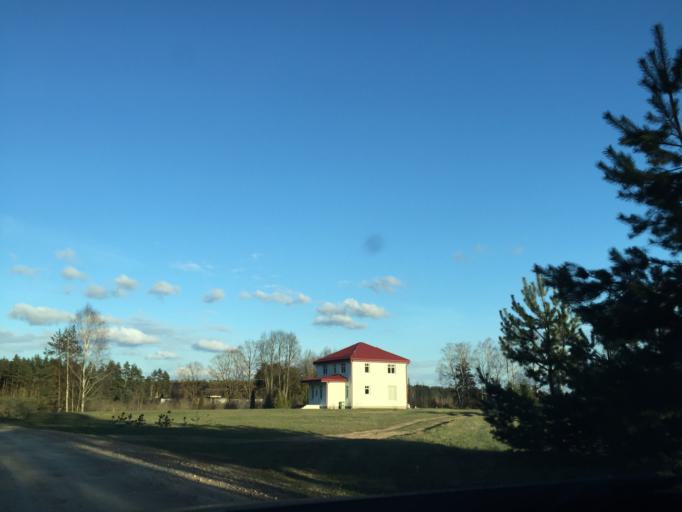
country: LV
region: Kekava
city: Kekava
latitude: 56.8636
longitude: 24.2107
